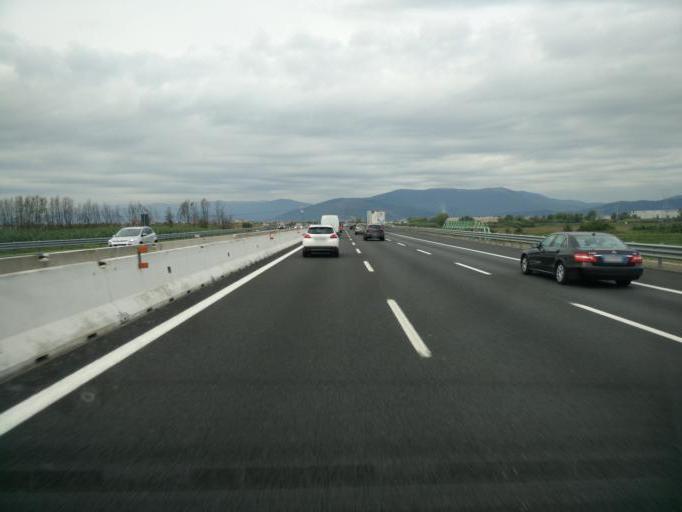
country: IT
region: Tuscany
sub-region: Province of Florence
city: San Donnino
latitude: 43.8012
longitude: 11.1548
